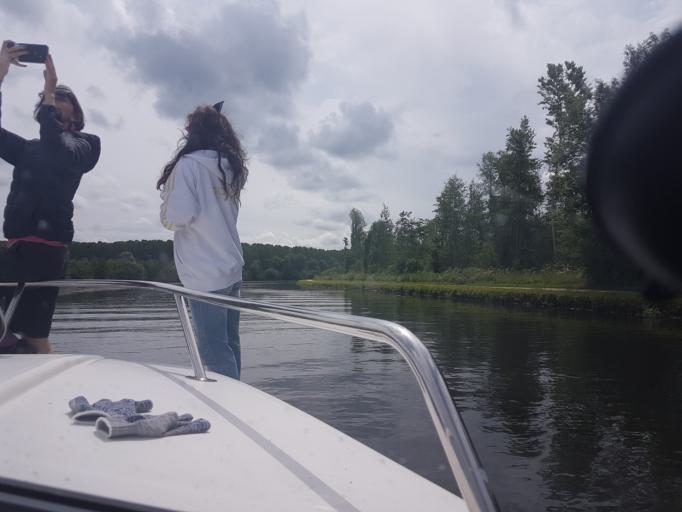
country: FR
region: Bourgogne
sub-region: Departement de l'Yonne
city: Augy
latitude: 47.7792
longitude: 3.6058
